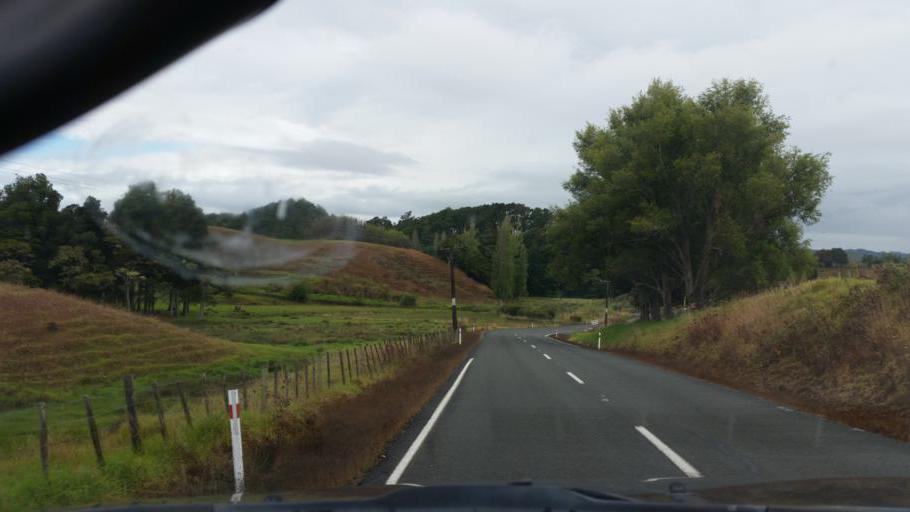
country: NZ
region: Auckland
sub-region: Auckland
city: Wellsford
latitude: -36.1237
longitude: 174.3609
